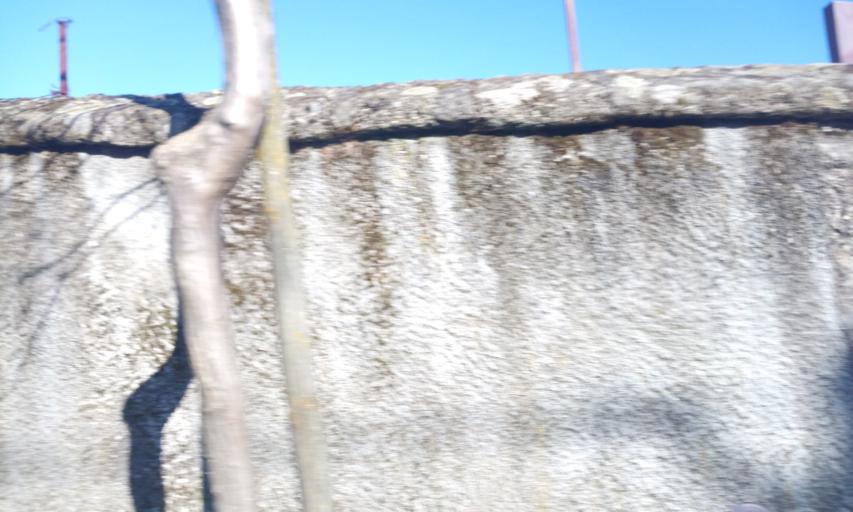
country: PT
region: Guarda
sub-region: Fornos de Algodres
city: Fornos de Algodres
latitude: 40.5154
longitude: -7.6090
